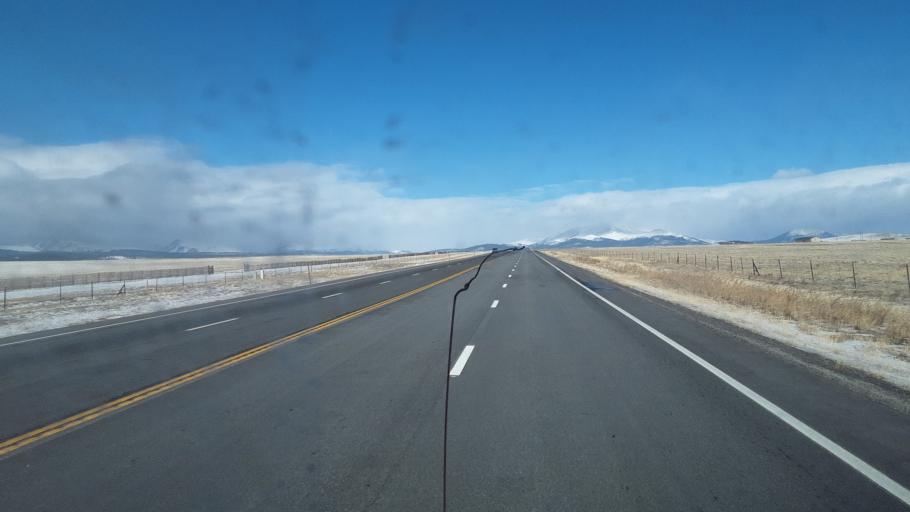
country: US
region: Colorado
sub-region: Park County
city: Fairplay
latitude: 39.1348
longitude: -105.9955
